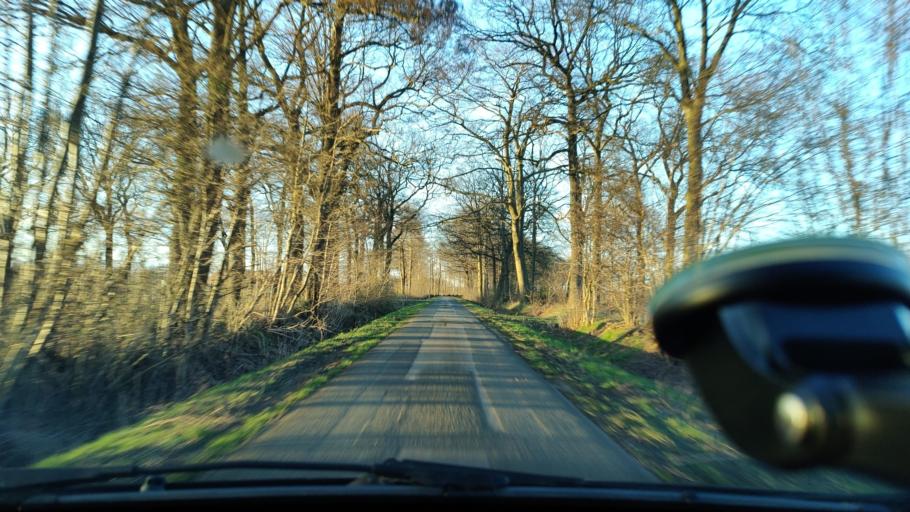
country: DE
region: North Rhine-Westphalia
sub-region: Regierungsbezirk Munster
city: Coesfeld
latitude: 51.8442
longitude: 7.1634
